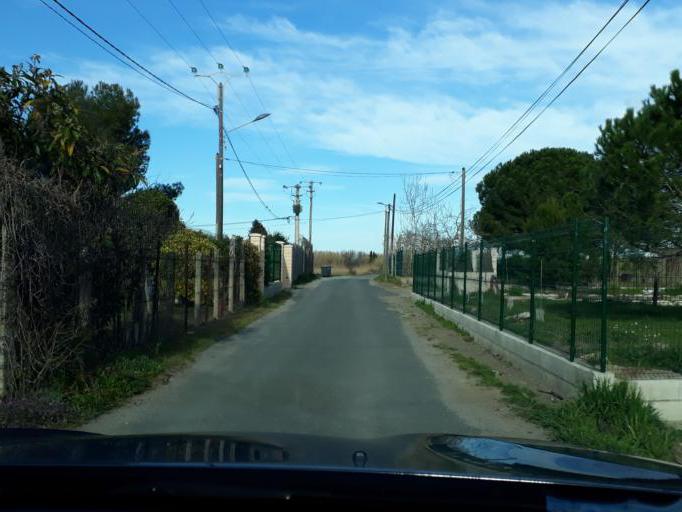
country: FR
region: Languedoc-Roussillon
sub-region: Departement de l'Herault
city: Marseillan
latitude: 43.3315
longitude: 3.5530
